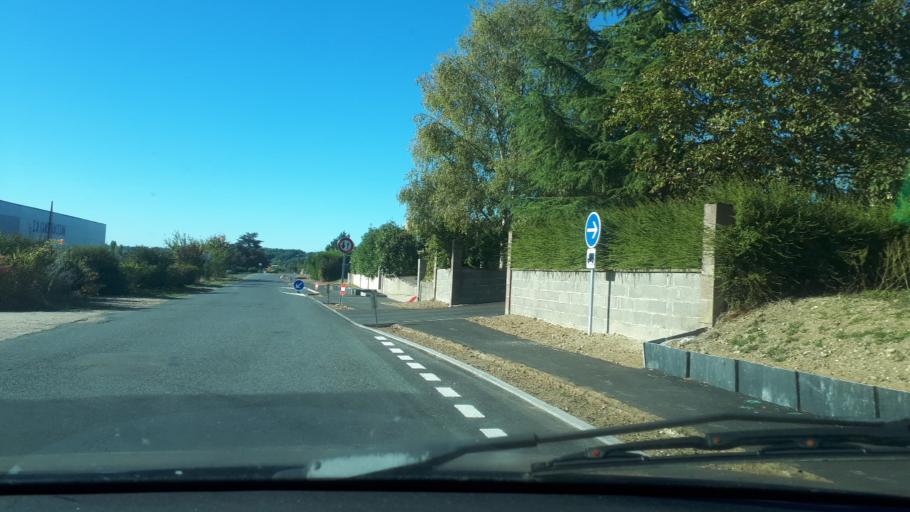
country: FR
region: Centre
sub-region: Departement du Loir-et-Cher
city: Villiers-sur-Loir
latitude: 47.8004
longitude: 1.0025
